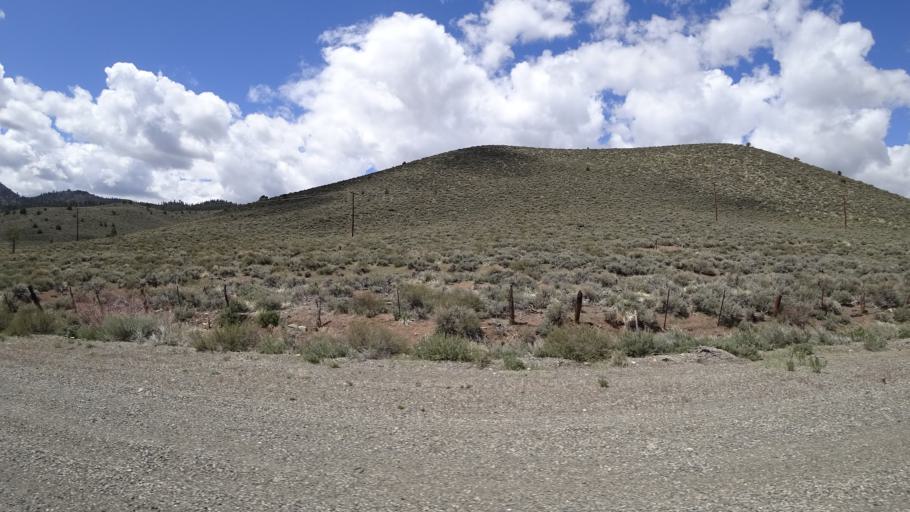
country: US
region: California
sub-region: Mono County
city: Bridgeport
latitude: 38.3059
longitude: -119.3140
